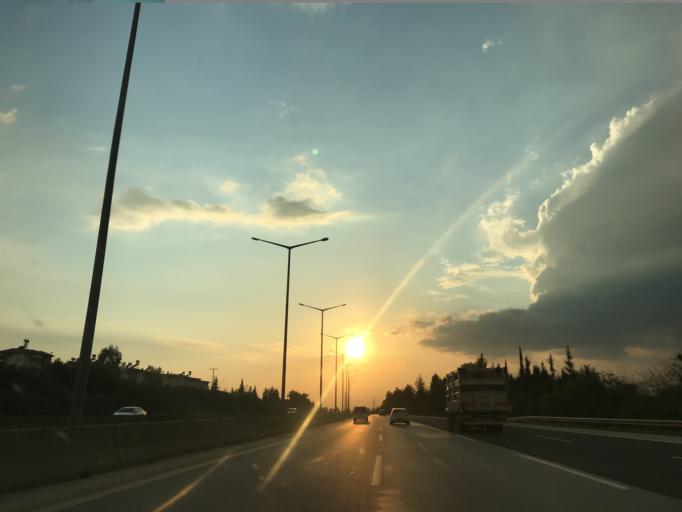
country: TR
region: Adana
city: Seyhan
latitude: 37.0318
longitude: 35.2378
